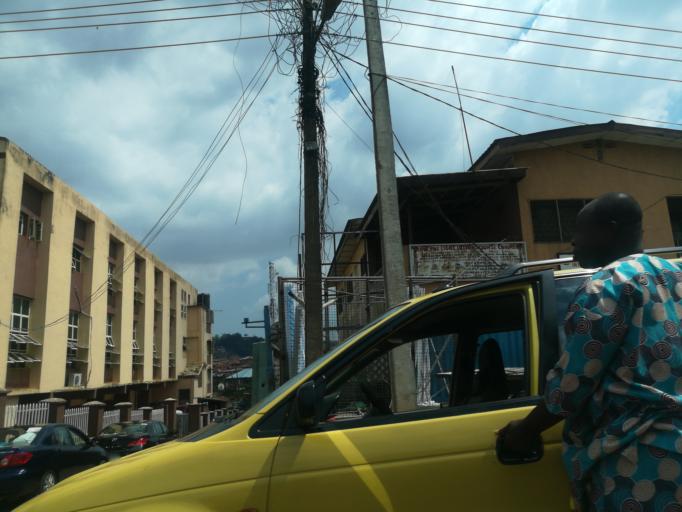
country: NG
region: Oyo
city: Ibadan
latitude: 7.3910
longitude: 3.8866
